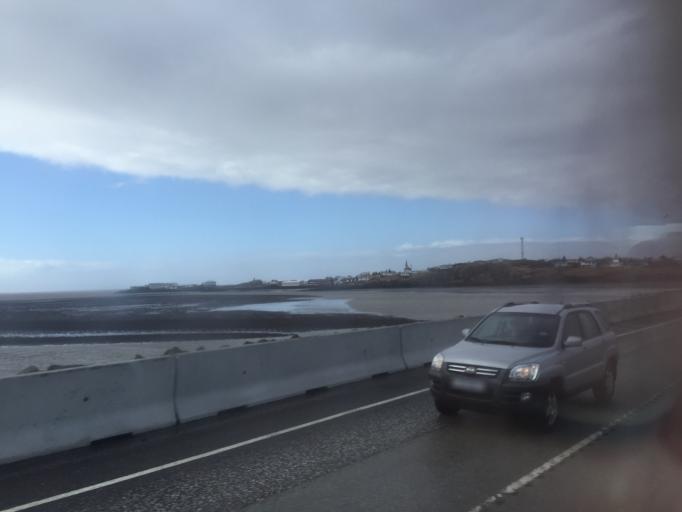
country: IS
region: West
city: Borgarnes
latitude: 64.5368
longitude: -21.9006
